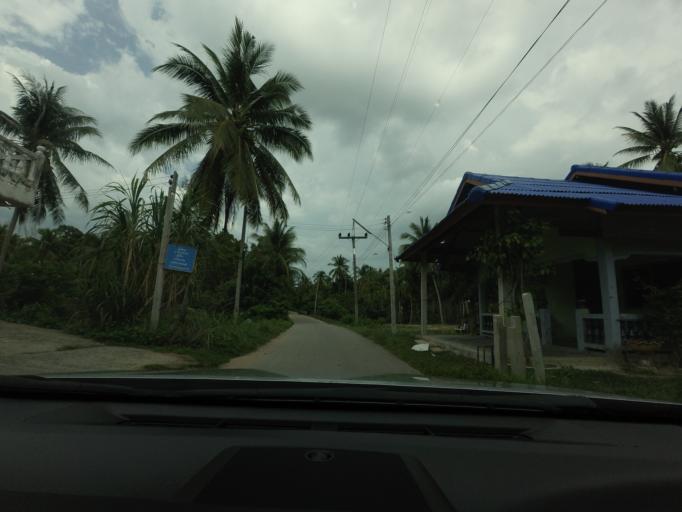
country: TH
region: Songkhla
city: Chana
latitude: 6.9499
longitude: 100.8319
